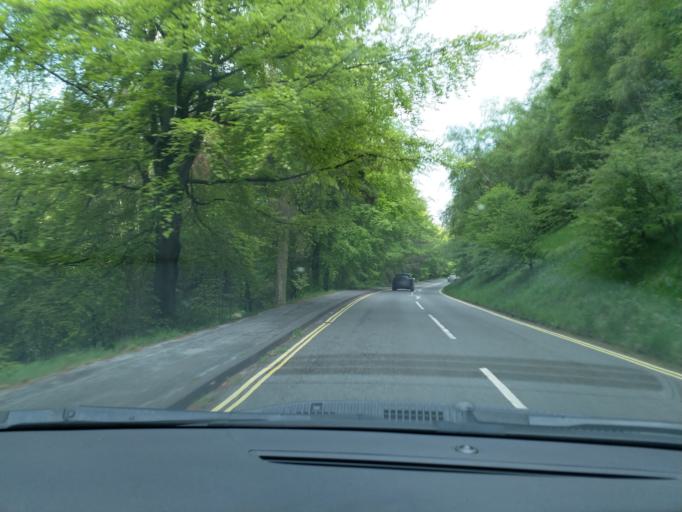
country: GB
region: England
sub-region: Derbyshire
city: Hope Valley
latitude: 53.3879
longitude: -1.7220
